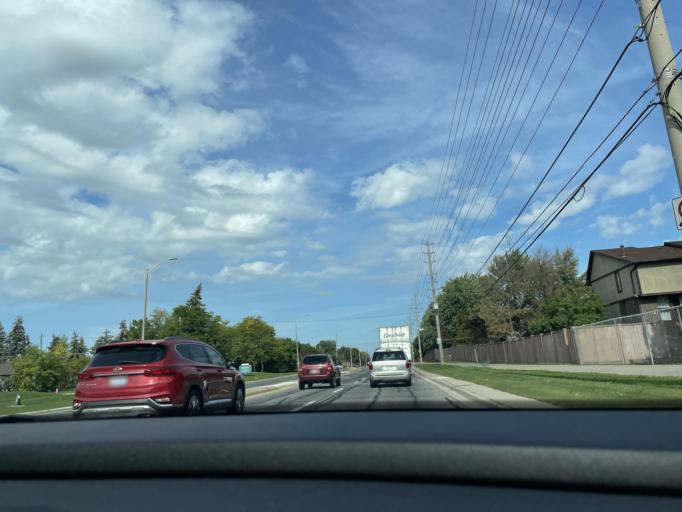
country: CA
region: Ontario
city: Brampton
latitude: 43.5834
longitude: -79.7643
